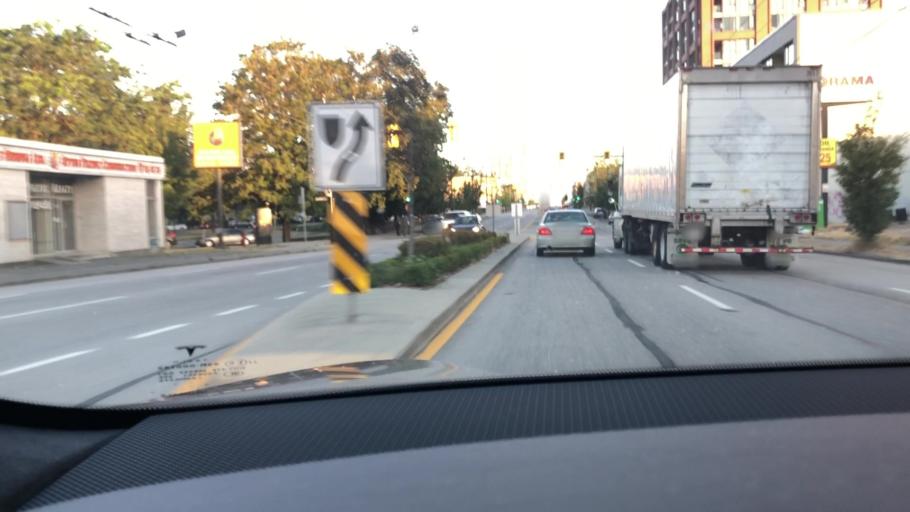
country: CA
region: British Columbia
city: Vancouver
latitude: 49.2380
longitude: -123.0496
